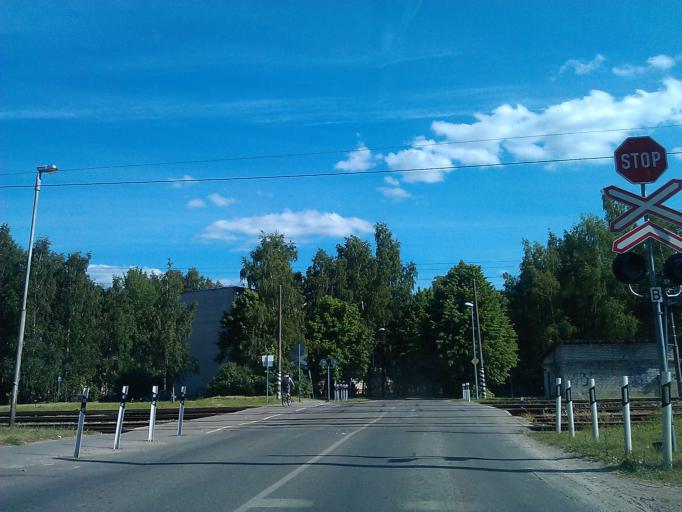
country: LV
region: Riga
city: Bergi
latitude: 56.9936
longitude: 24.2389
